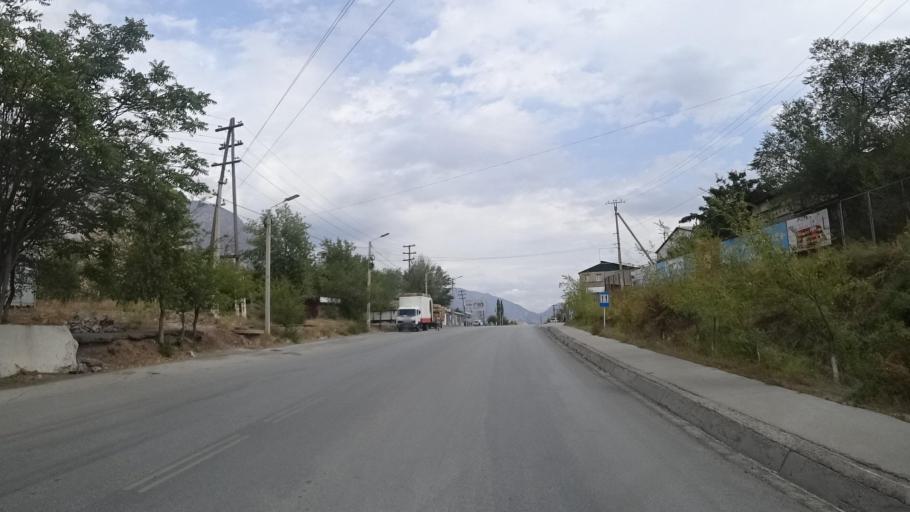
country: KG
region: Jalal-Abad
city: Toktogul
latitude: 41.6305
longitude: 72.6849
